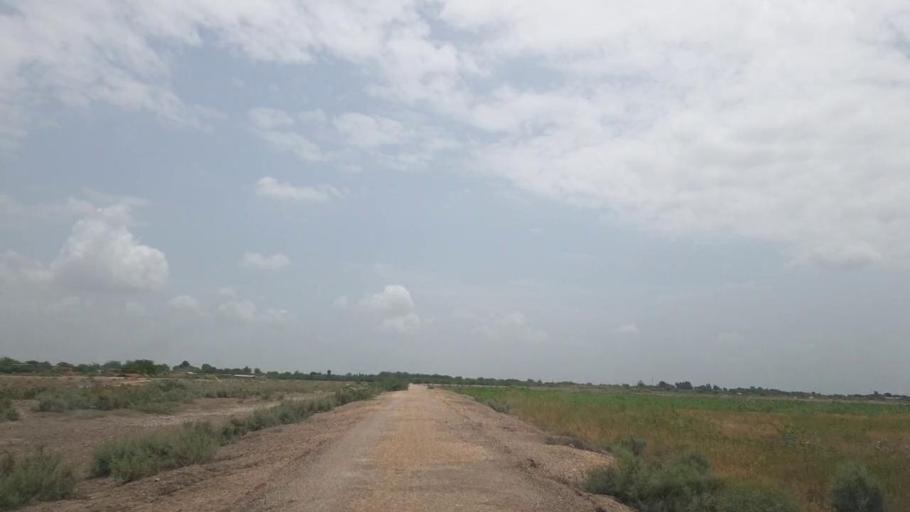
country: PK
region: Sindh
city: Naukot
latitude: 24.9135
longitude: 69.2031
